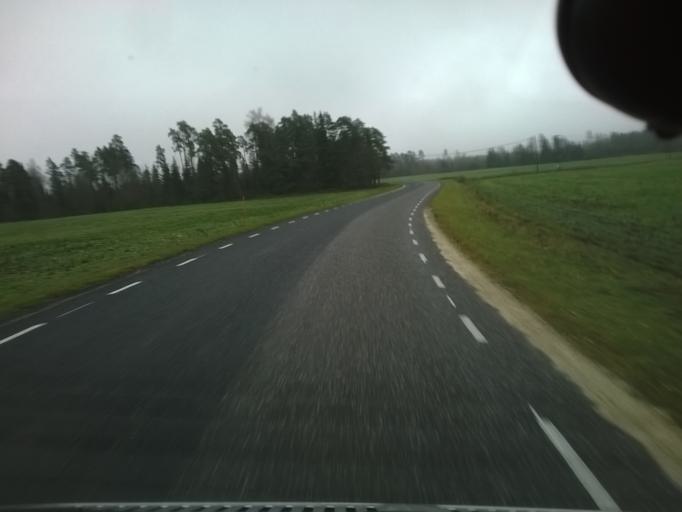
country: EE
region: Harju
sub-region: Saue linn
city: Saue
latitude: 59.1443
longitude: 24.5524
